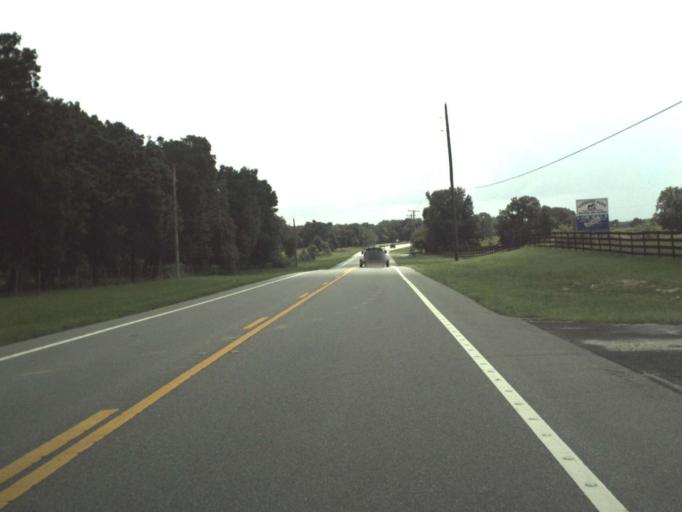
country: US
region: Florida
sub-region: Sumter County
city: Lake Panasoffkee
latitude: 28.7220
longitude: -82.0868
